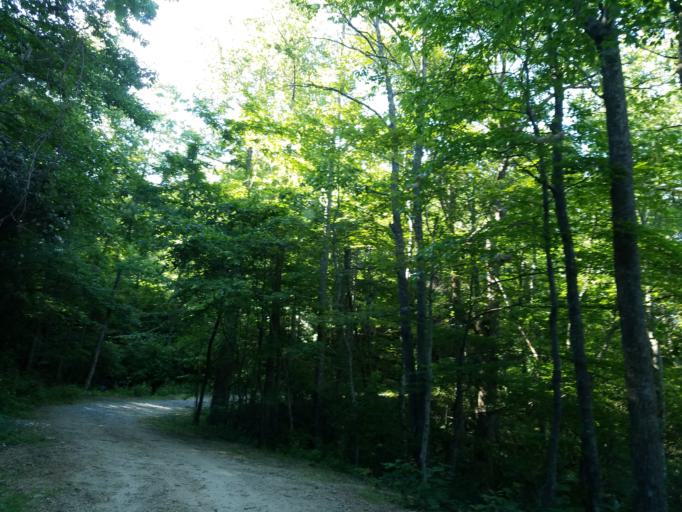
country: US
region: Georgia
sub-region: Dawson County
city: Dawsonville
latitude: 34.5989
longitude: -84.2112
